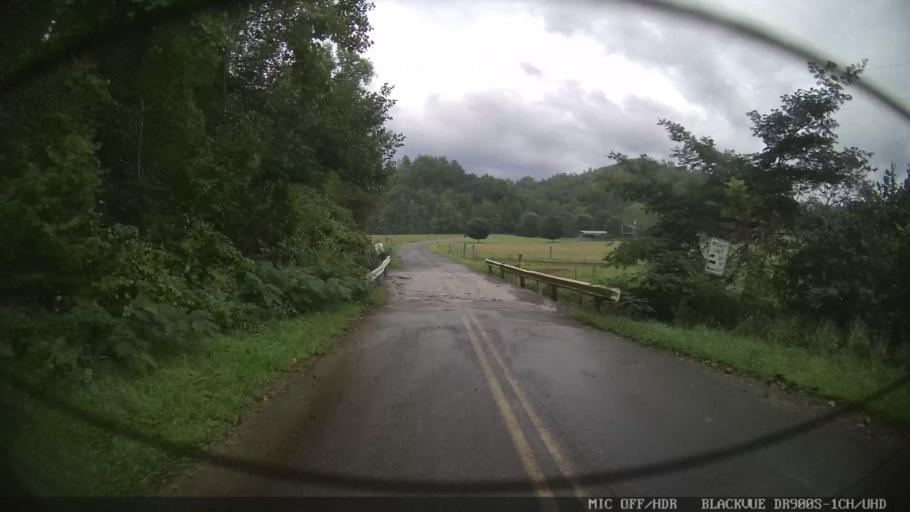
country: US
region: Georgia
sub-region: Gilmer County
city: Ellijay
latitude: 34.8014
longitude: -84.5652
